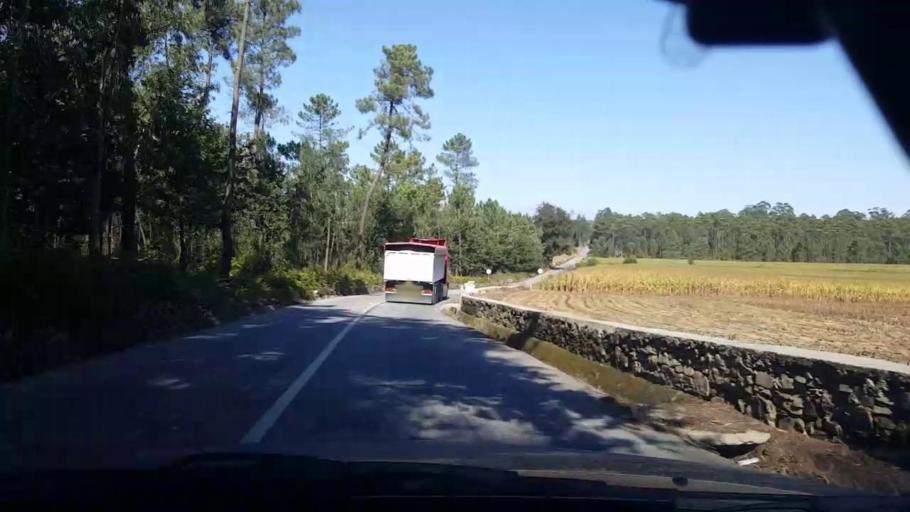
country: PT
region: Braga
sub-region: Vila Nova de Famalicao
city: Ribeirao
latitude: 41.3648
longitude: -8.6221
